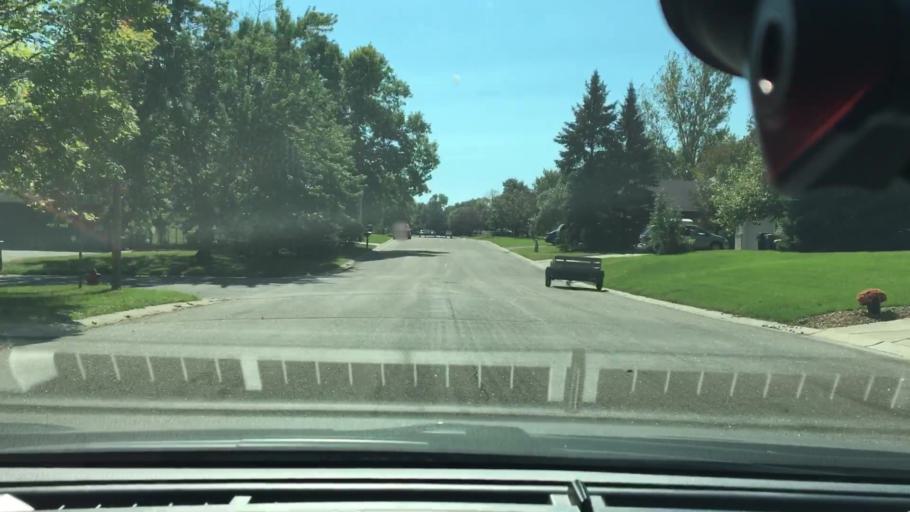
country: US
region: Minnesota
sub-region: Wright County
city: Saint Michael
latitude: 45.2027
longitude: -93.6745
